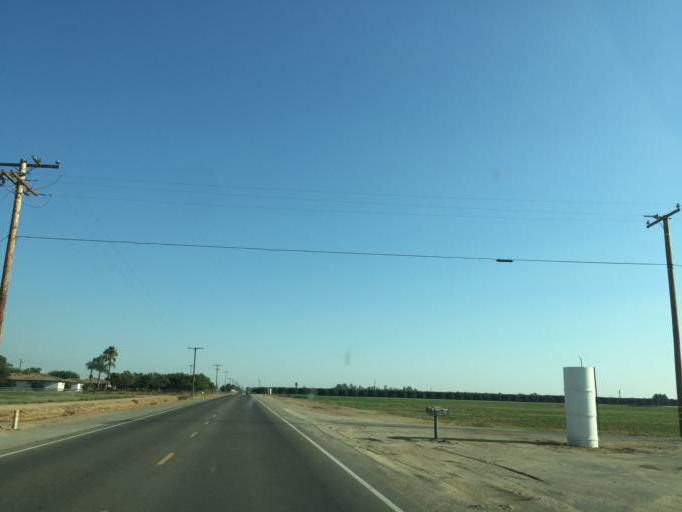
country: US
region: California
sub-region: Tulare County
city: Cutler
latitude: 36.4507
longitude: -119.2777
